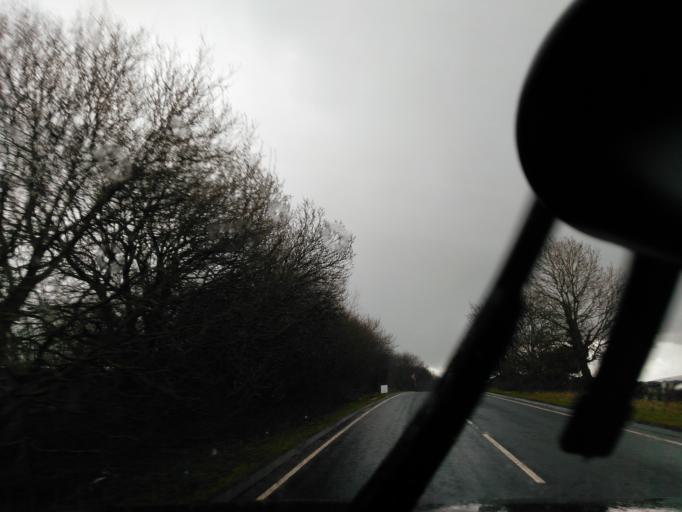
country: GB
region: England
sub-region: North Yorkshire
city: Embsay
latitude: 53.9719
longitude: -1.9738
